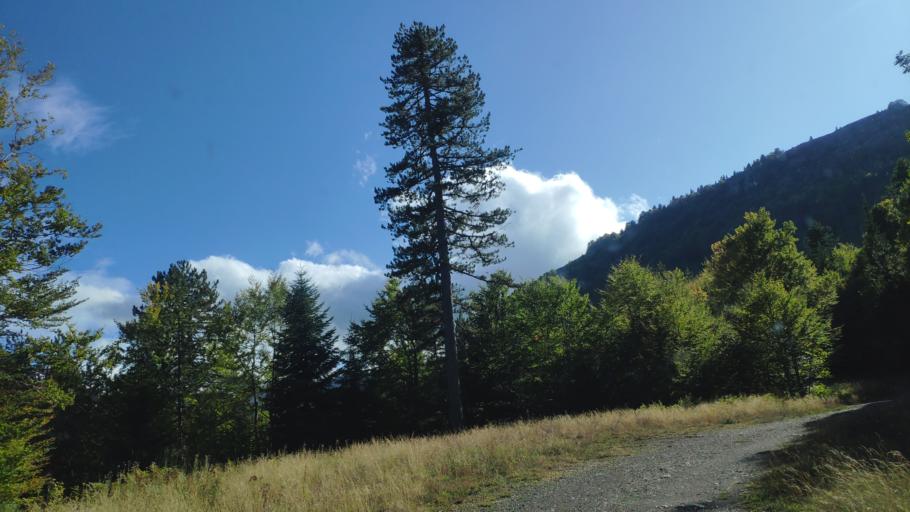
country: AL
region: Korce
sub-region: Rrethi i Devollit
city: Miras
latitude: 40.3657
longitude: 20.8982
